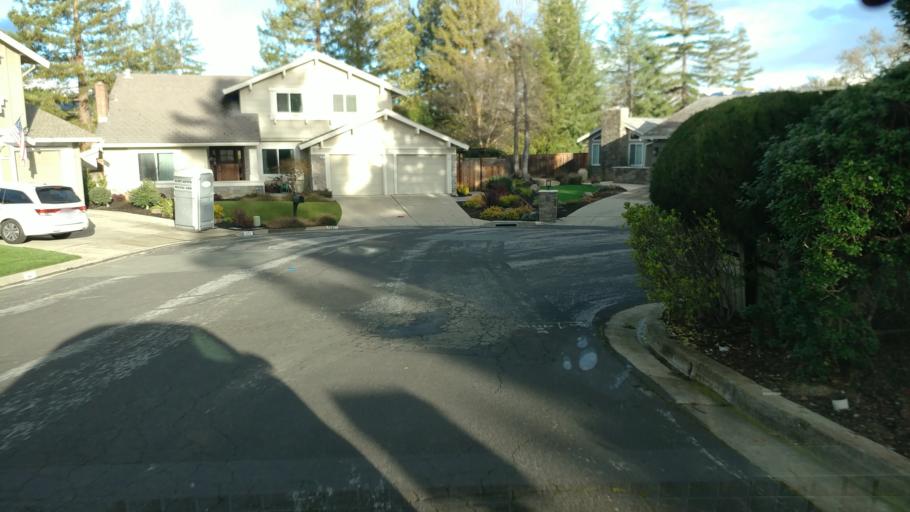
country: US
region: California
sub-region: Contra Costa County
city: Danville
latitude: 37.8300
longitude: -121.9957
